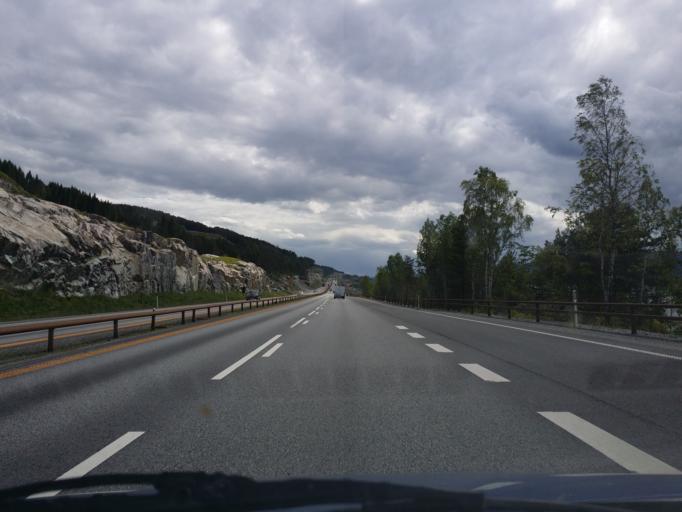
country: NO
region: Hedmark
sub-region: Stange
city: Stange
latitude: 60.5354
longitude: 11.2439
